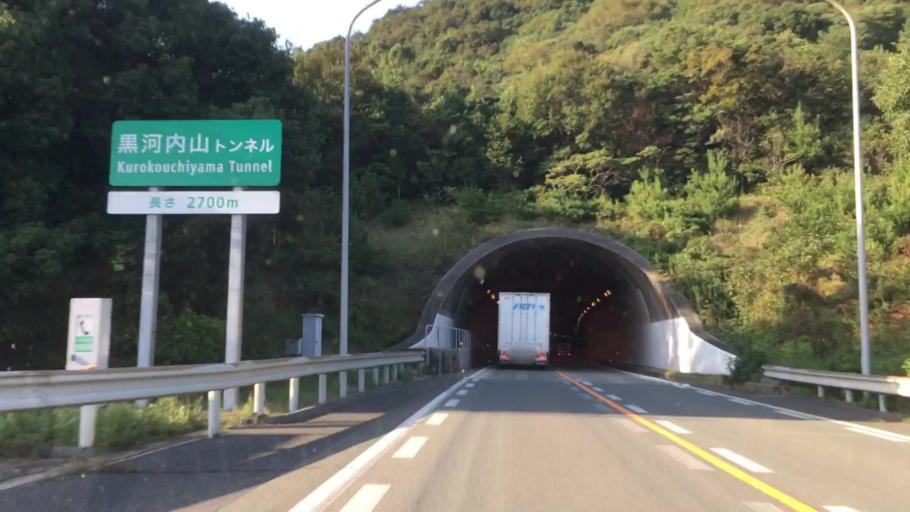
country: JP
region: Yamaguchi
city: Ogori-shimogo
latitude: 34.1003
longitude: 131.4510
